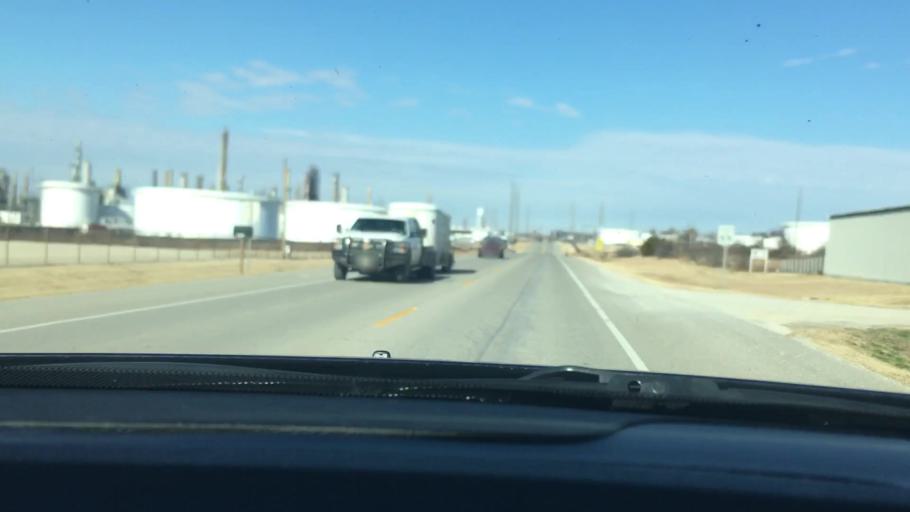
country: US
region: Oklahoma
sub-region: Garvin County
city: Wynnewood
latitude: 34.6276
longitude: -97.1644
